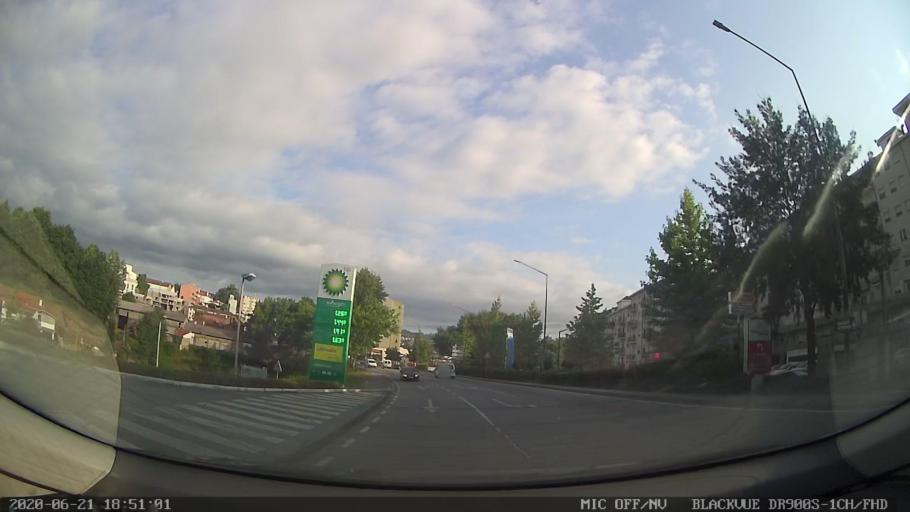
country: PT
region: Porto
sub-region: Amarante
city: Amarante
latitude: 41.2750
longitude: -8.0825
